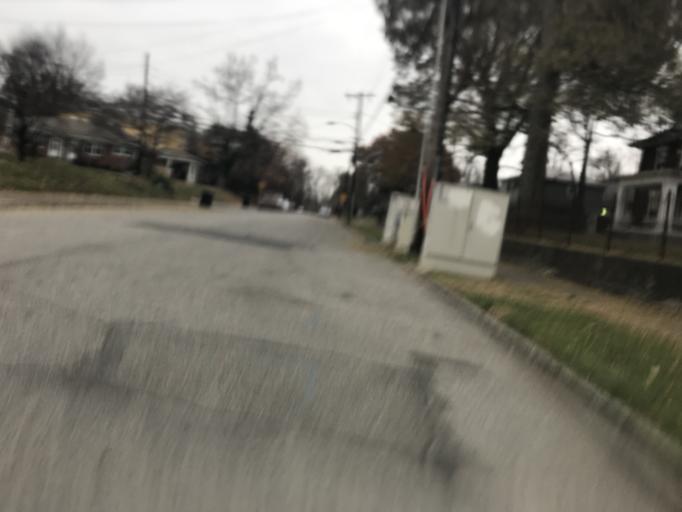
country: US
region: Indiana
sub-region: Clark County
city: Jeffersonville
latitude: 38.2560
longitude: -85.7075
